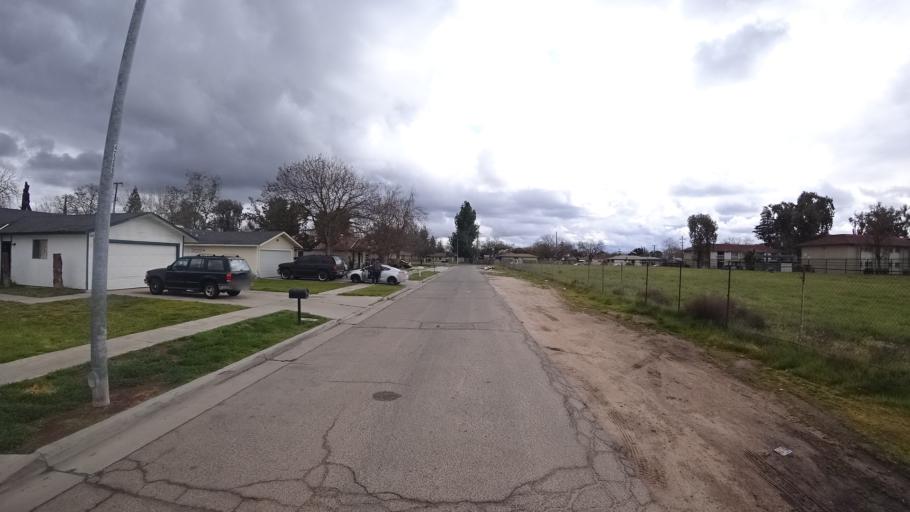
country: US
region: California
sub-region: Fresno County
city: West Park
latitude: 36.7846
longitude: -119.8412
